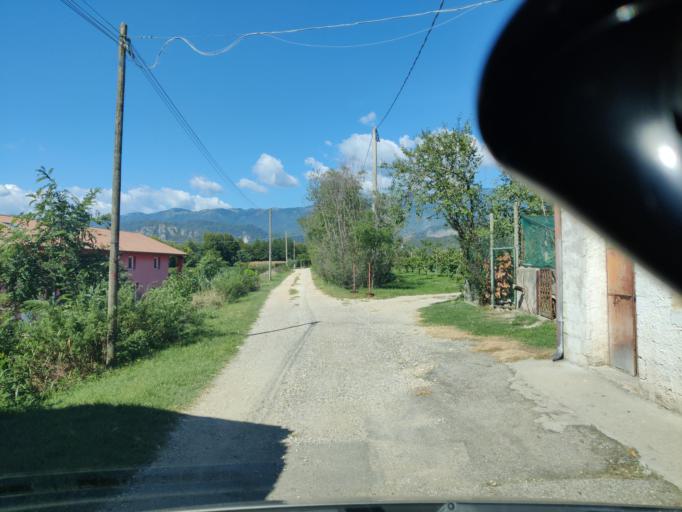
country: IT
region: Veneto
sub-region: Provincia di Treviso
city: Cappella Maggiore
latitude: 45.9714
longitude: 12.3365
